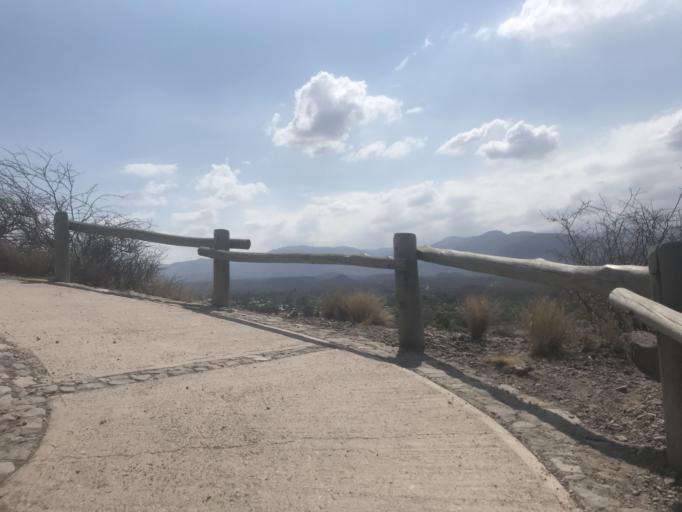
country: AR
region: Mendoza
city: Mendoza
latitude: -32.8855
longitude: -68.8897
